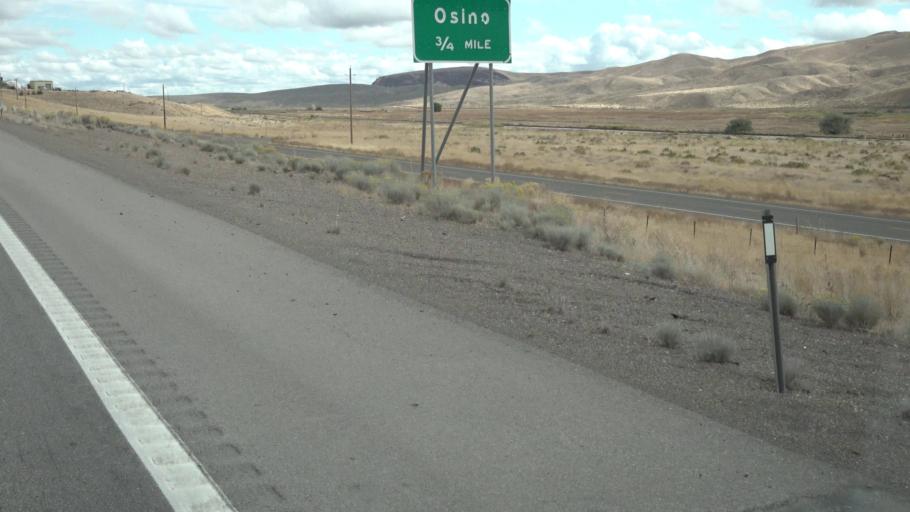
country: US
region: Nevada
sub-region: Elko County
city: Elko
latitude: 40.9247
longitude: -115.6790
